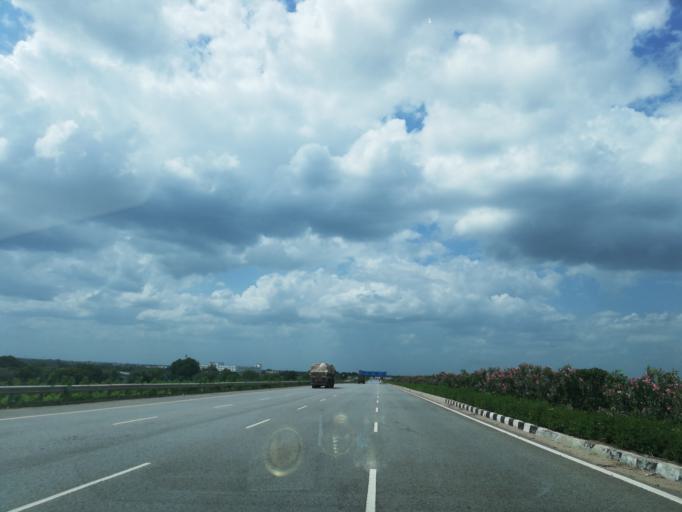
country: IN
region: Telangana
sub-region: Medak
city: Serilingampalle
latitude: 17.4459
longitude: 78.2563
